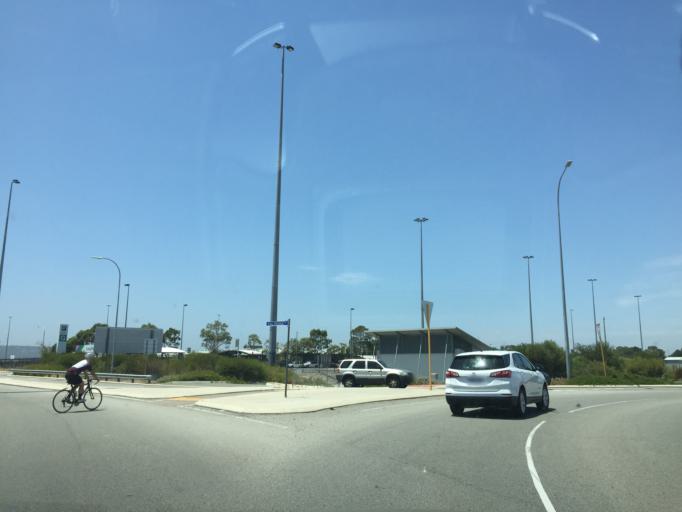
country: AU
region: Western Australia
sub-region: Belmont
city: Redcliffe
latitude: -31.9553
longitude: 115.9695
